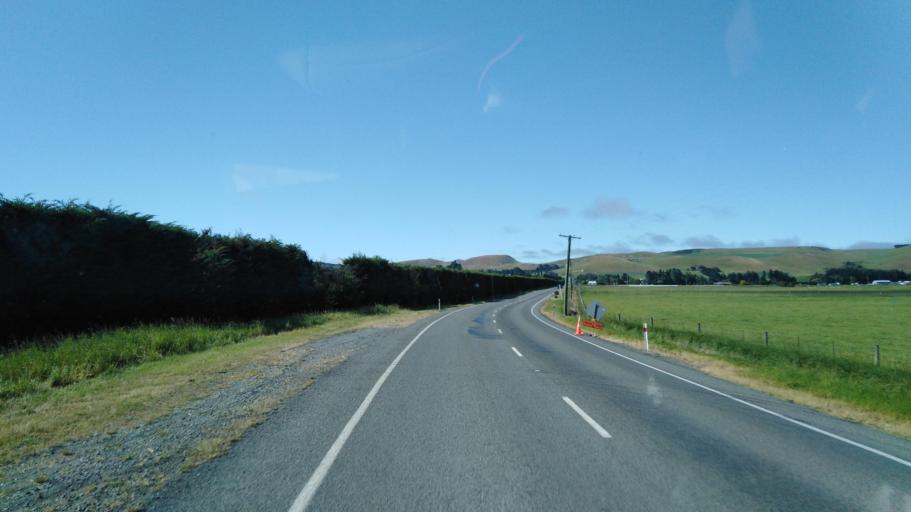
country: NZ
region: Canterbury
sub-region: Hurunui District
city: Amberley
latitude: -42.9556
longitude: 172.7092
